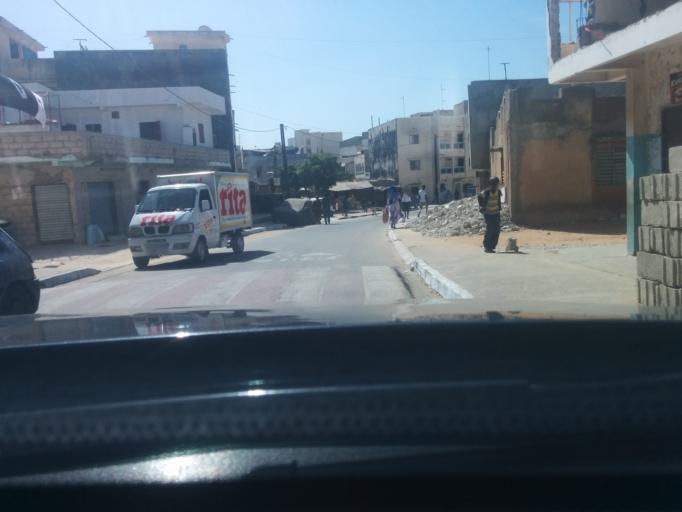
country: SN
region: Dakar
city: Pikine
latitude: 14.7579
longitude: -17.4311
